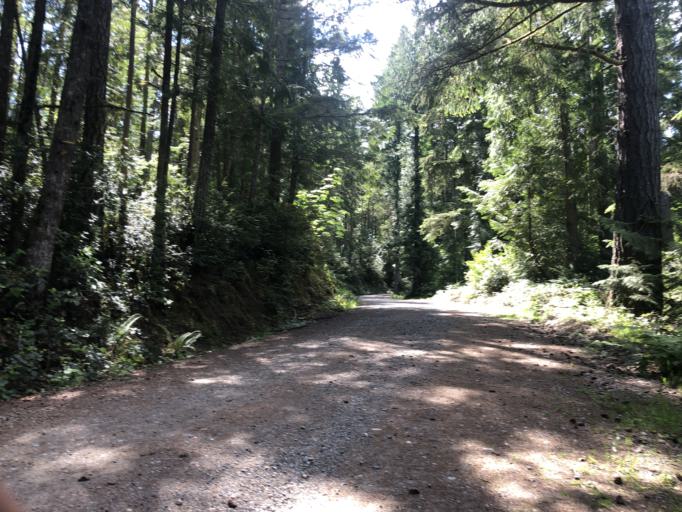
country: US
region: Washington
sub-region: Kitsap County
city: Erlands Point-Kitsap Lake
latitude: 47.5796
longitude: -122.7193
